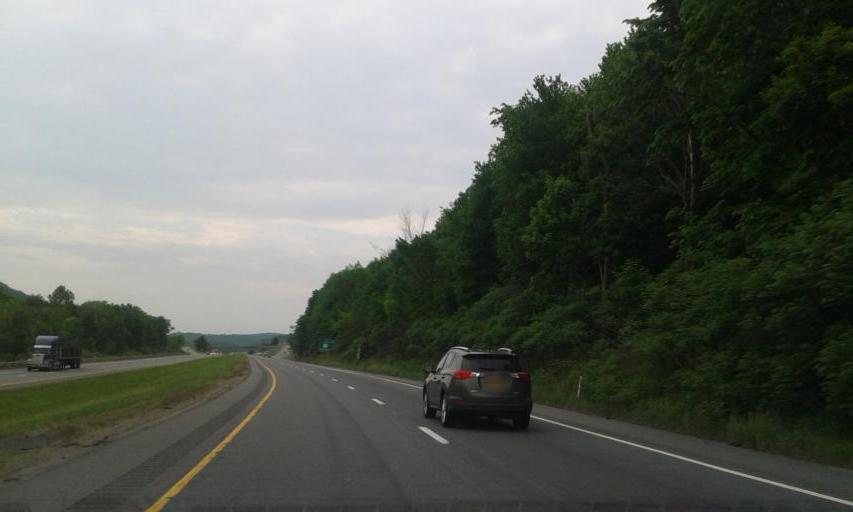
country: US
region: Pennsylvania
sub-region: Susquehanna County
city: Susquehanna
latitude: 41.7793
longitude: -75.6834
